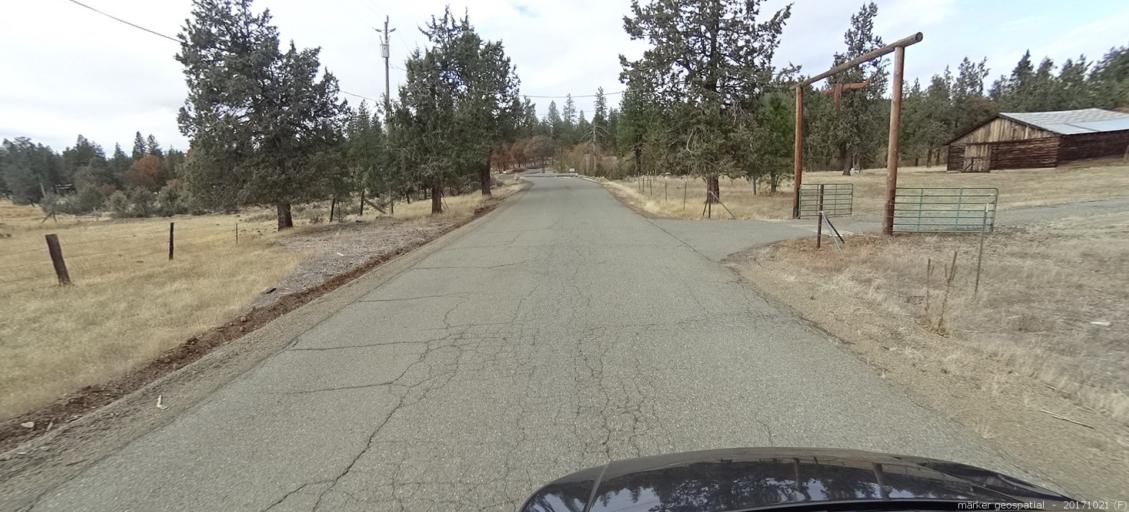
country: US
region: California
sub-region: Shasta County
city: Burney
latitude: 40.9266
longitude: -121.6486
